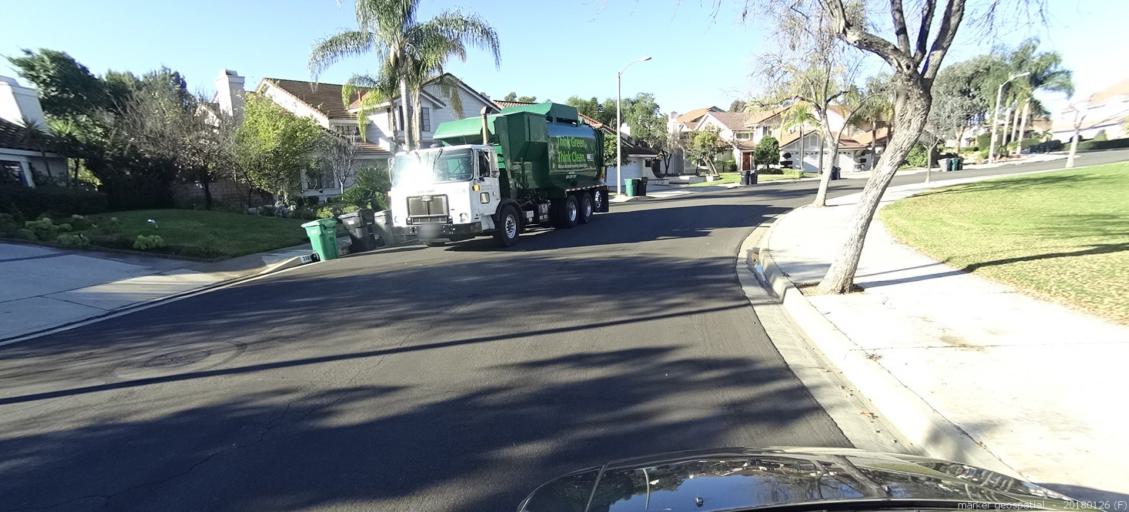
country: US
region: California
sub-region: Los Angeles County
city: Walnut
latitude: 33.9852
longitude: -117.8508
